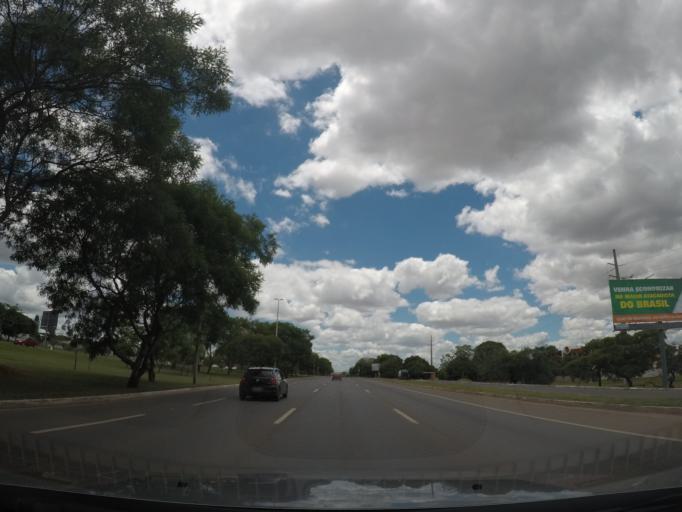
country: BR
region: Federal District
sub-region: Brasilia
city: Brasilia
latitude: -15.7656
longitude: -47.9330
